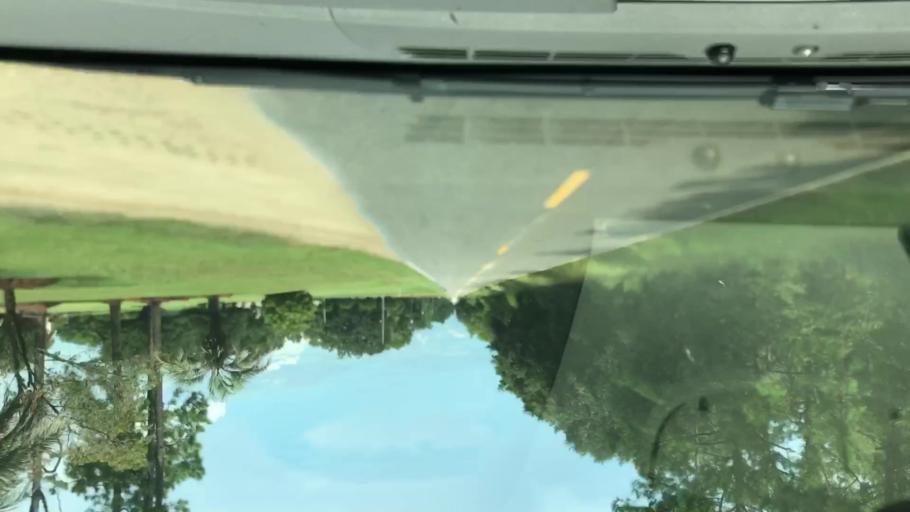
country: US
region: Georgia
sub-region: Seminole County
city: Donalsonville
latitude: 31.1169
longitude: -84.9957
